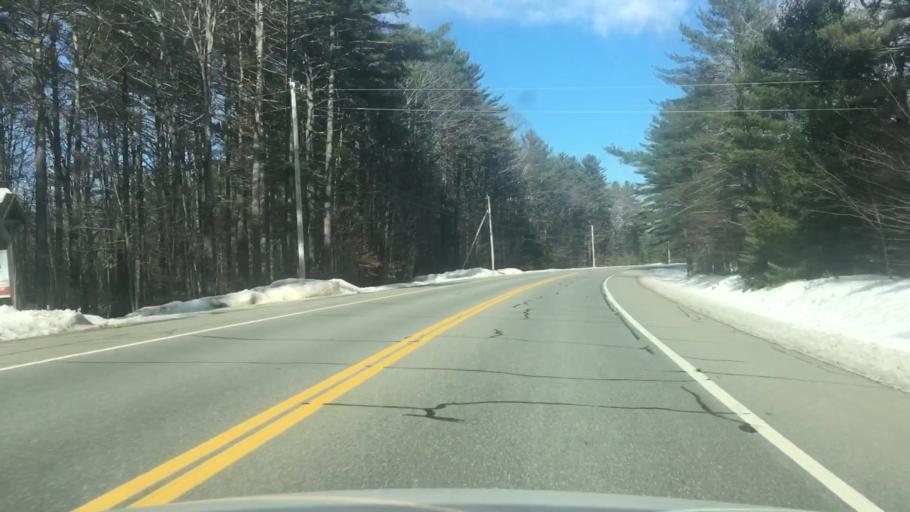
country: US
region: Maine
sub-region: Somerset County
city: Madison
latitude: 44.9811
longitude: -69.8674
